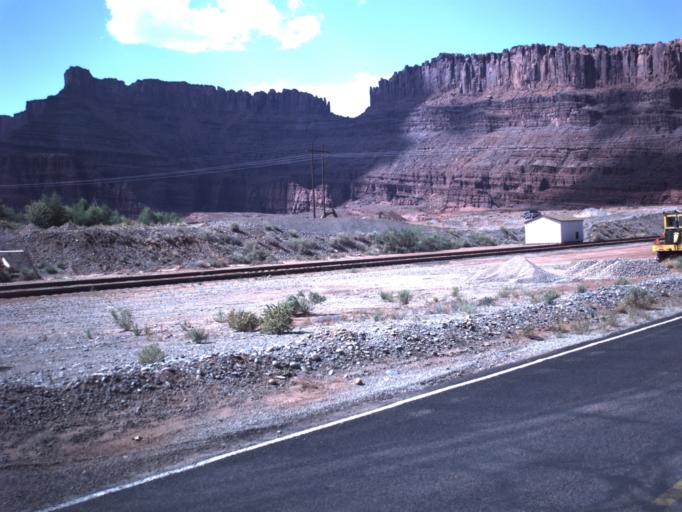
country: US
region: Utah
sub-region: Grand County
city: Moab
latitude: 38.5242
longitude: -109.6543
